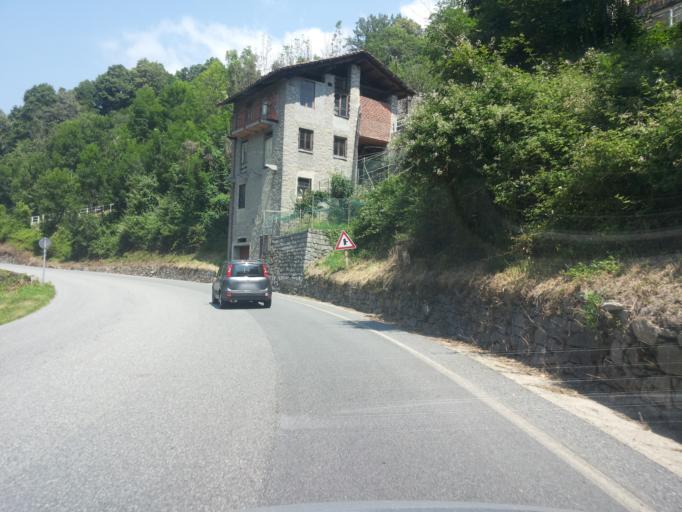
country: IT
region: Piedmont
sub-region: Provincia di Biella
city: Sagliano Micca
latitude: 45.6340
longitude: 8.0354
